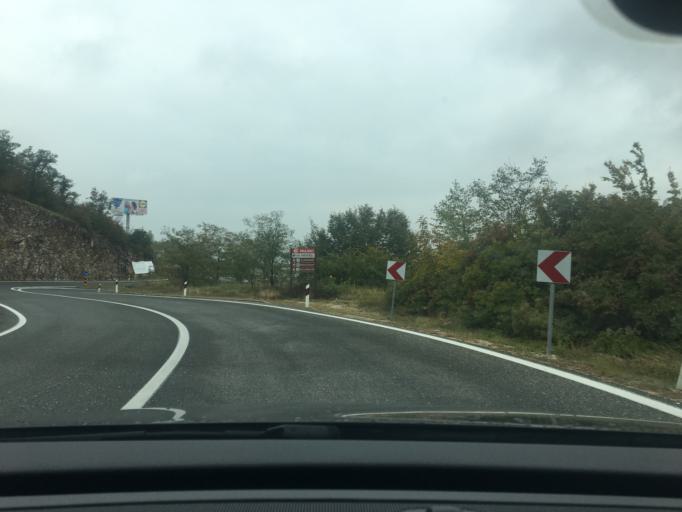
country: HR
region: Istarska
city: Buje
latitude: 45.4536
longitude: 13.6454
